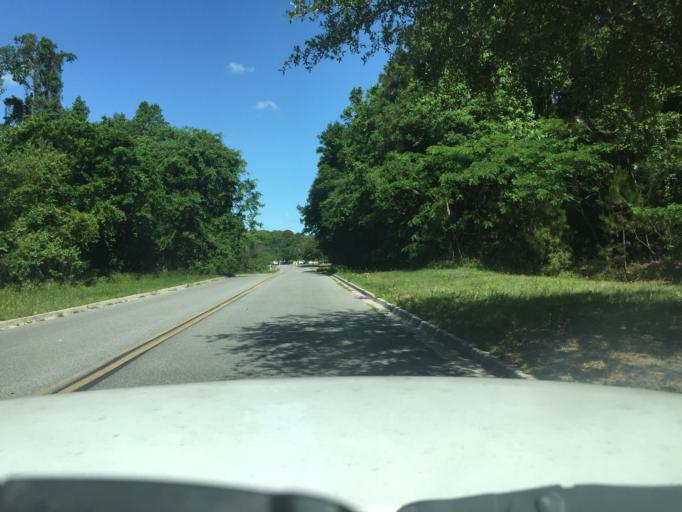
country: US
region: Georgia
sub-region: Chatham County
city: Isle of Hope
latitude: 32.0034
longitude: -81.0978
